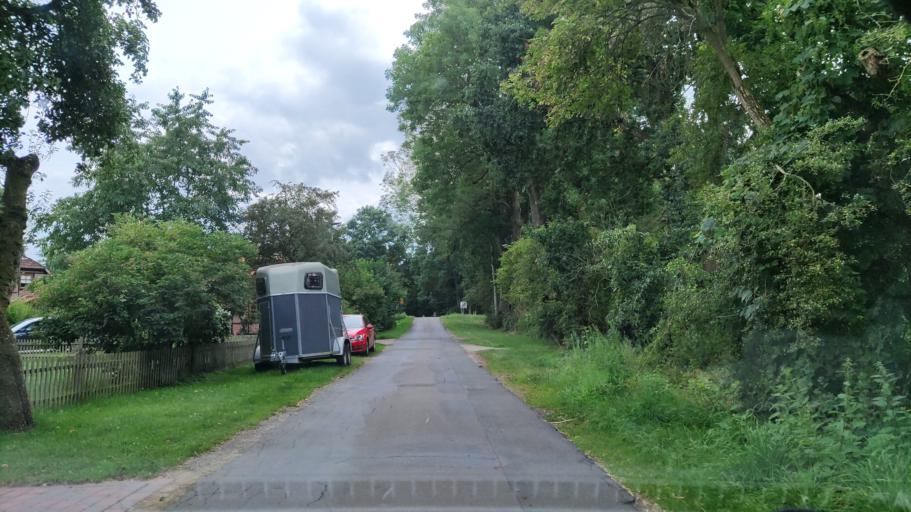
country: DE
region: Lower Saxony
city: Klein Gusborn
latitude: 53.0919
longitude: 11.1428
